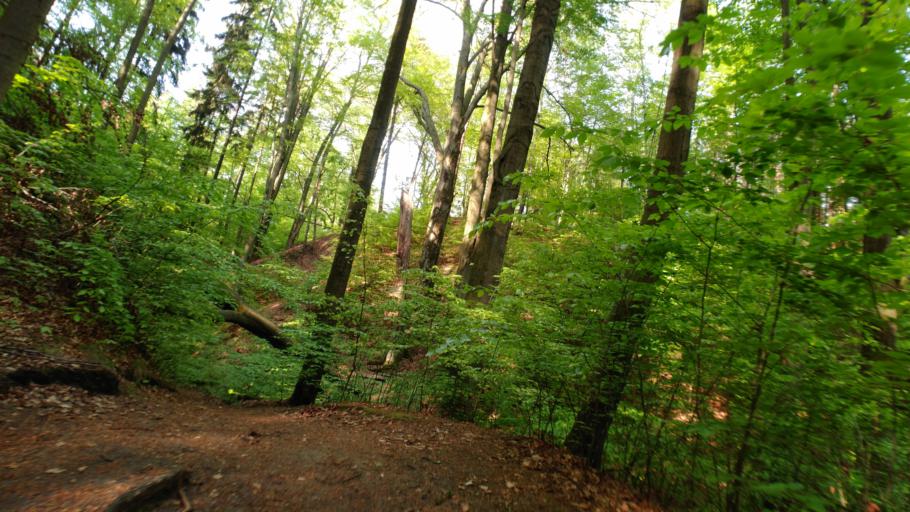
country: DE
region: Saxony
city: Albertstadt
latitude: 51.0783
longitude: 13.8090
